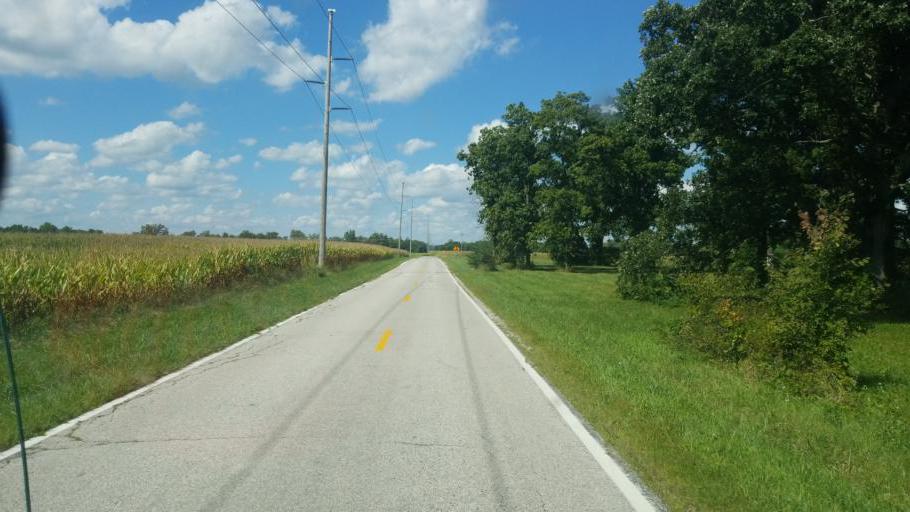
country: US
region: Ohio
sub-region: Marion County
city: Prospect
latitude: 40.3290
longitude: -83.2041
